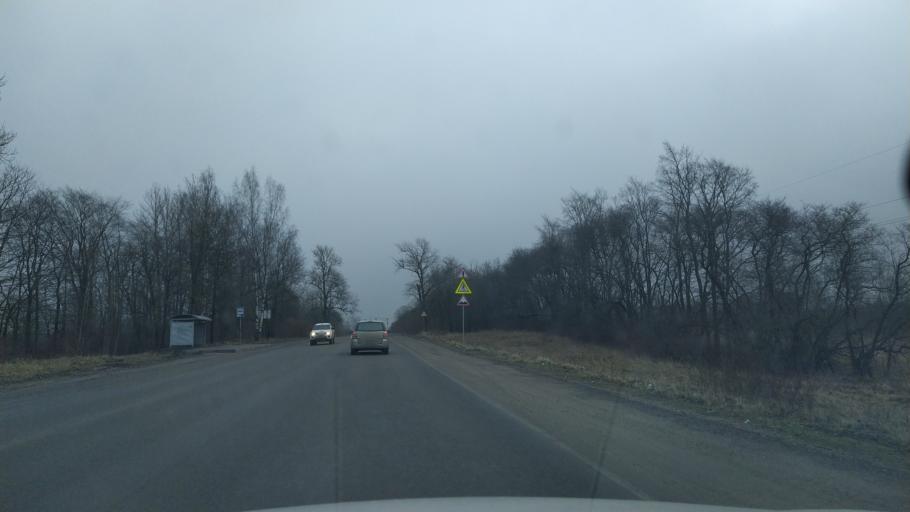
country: RU
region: St.-Petersburg
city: Gorelovo
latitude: 59.7296
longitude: 30.1506
